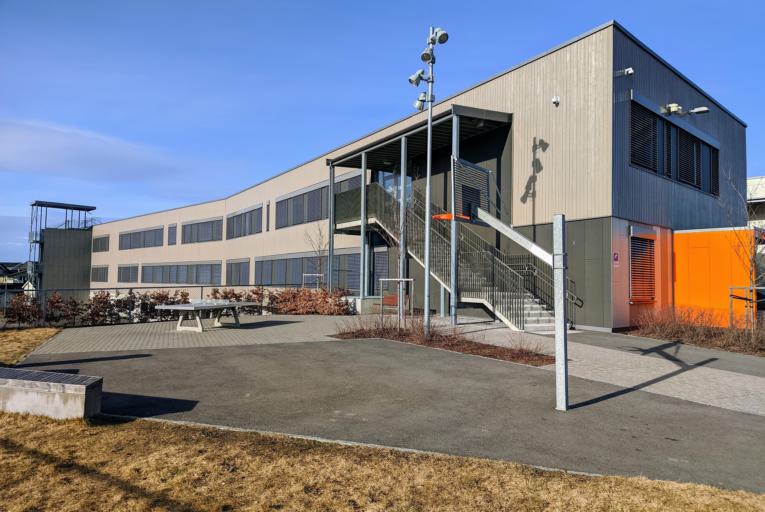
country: NO
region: Akershus
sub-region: Ullensaker
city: Jessheim
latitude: 60.1452
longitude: 11.1624
